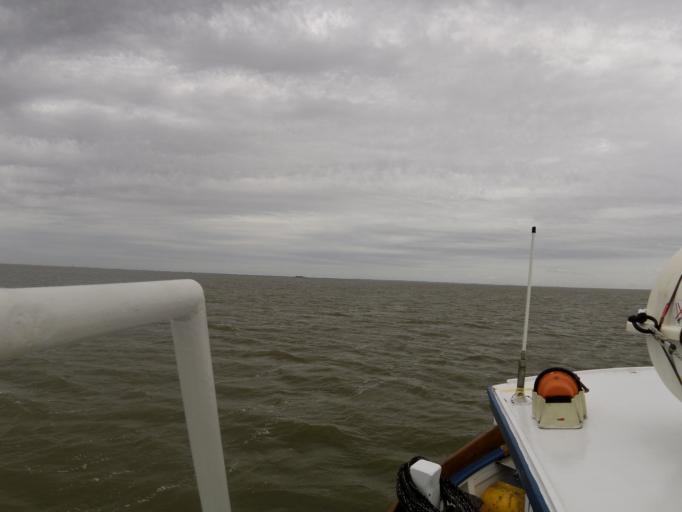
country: DE
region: Schleswig-Holstein
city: Langeness
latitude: 54.6156
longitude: 8.6494
